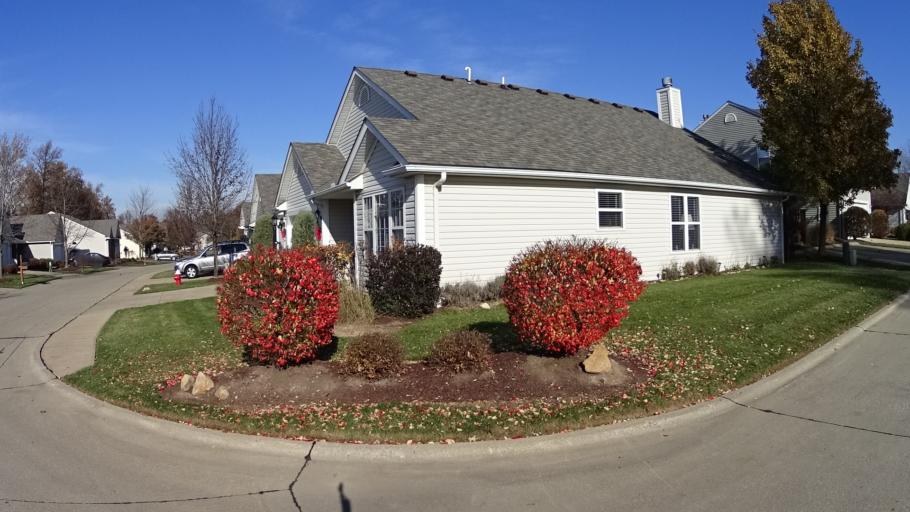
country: US
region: Ohio
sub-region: Lorain County
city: Avon Center
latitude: 41.4678
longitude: -82.0241
